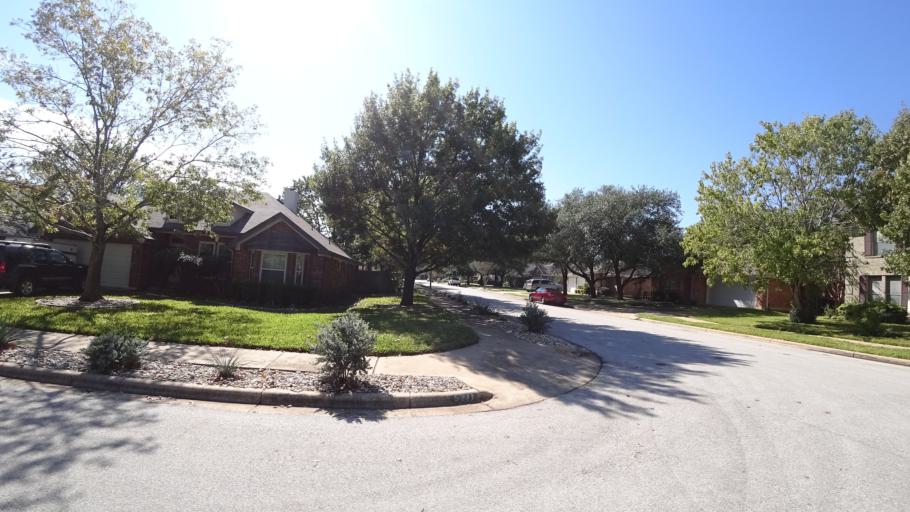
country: US
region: Texas
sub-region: Travis County
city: Shady Hollow
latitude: 30.2169
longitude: -97.8580
